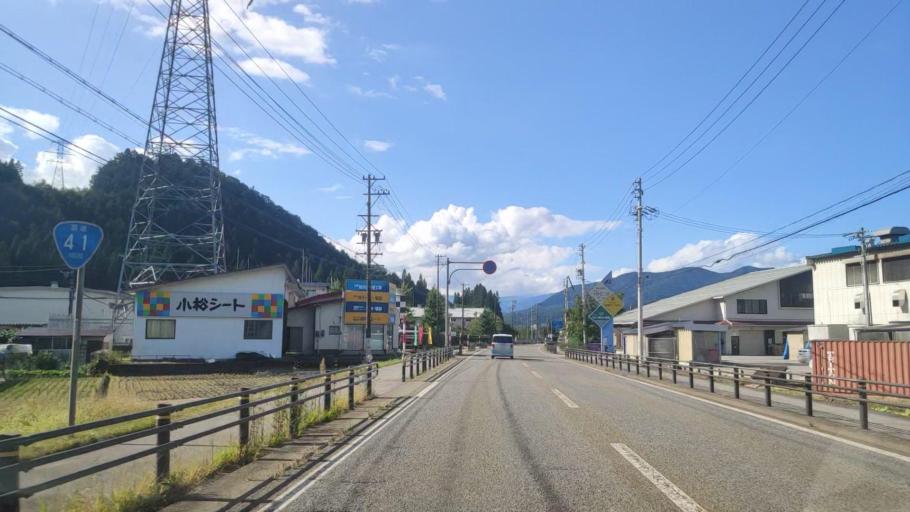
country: JP
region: Gifu
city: Takayama
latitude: 36.2376
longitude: 137.1759
